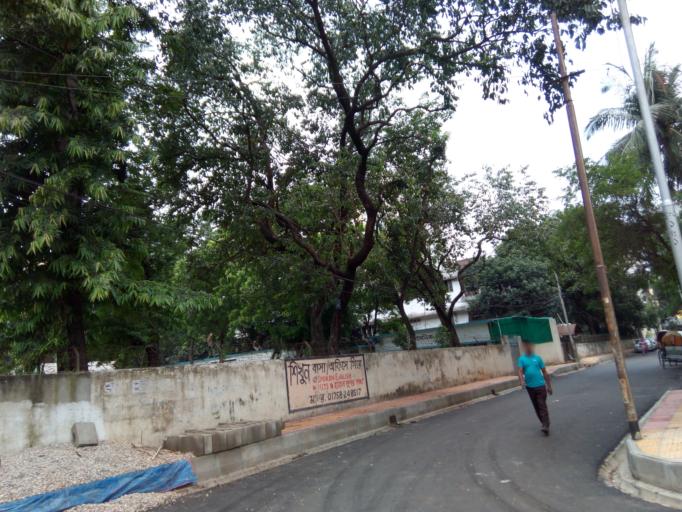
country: BD
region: Dhaka
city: Paltan
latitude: 23.7896
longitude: 90.4027
